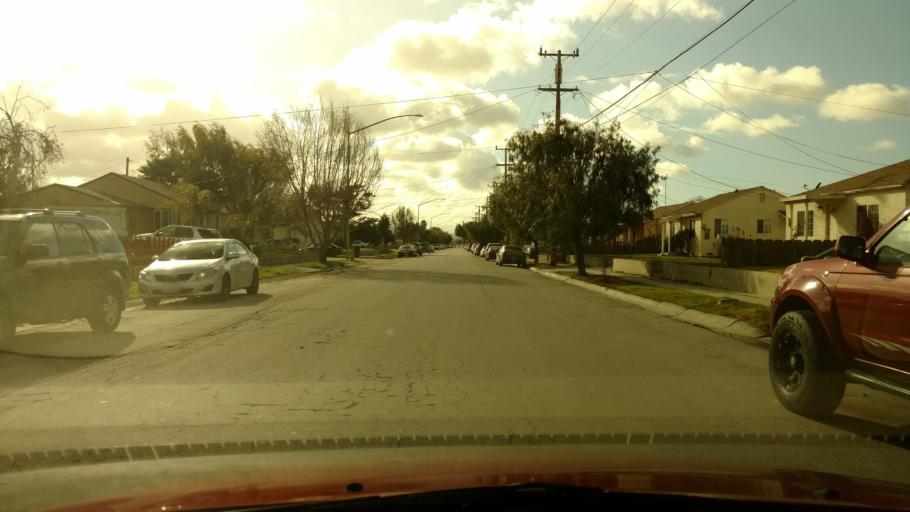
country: US
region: California
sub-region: Monterey County
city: Salinas
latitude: 36.6774
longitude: -121.6086
